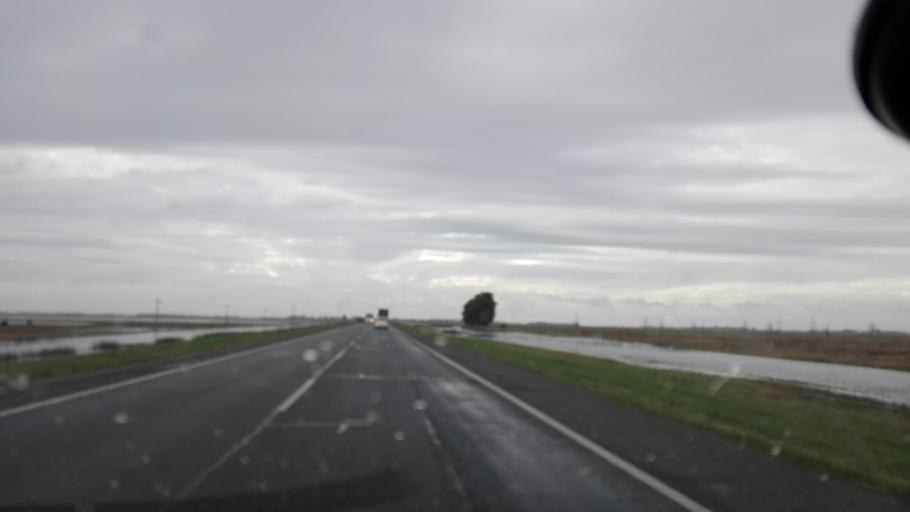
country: AR
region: Buenos Aires
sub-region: Partido de Las Flores
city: Las Flores
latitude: -35.7509
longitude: -58.9244
